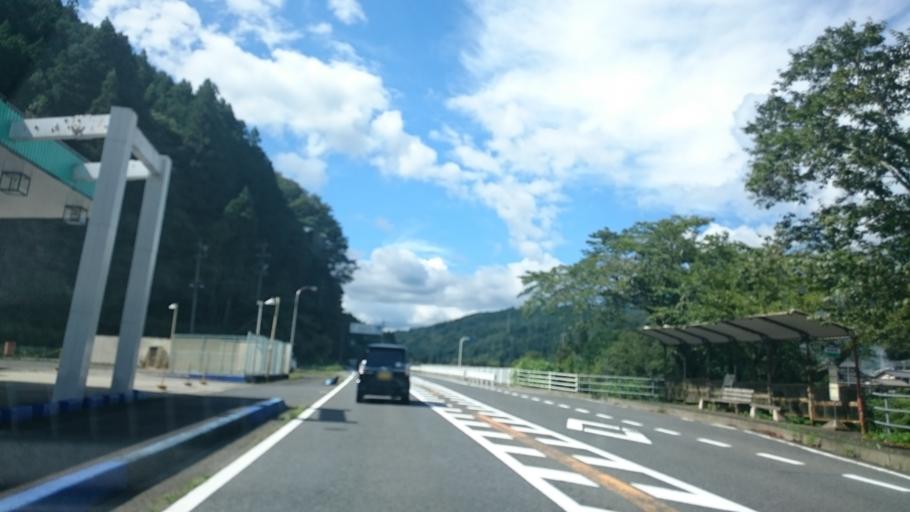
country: JP
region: Gifu
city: Nakatsugawa
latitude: 35.6215
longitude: 137.4619
